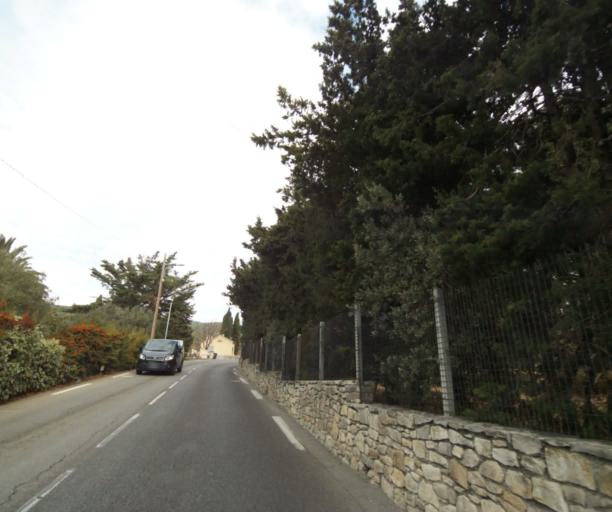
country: FR
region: Provence-Alpes-Cote d'Azur
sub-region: Departement des Bouches-du-Rhone
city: Ceyreste
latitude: 43.2190
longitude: 5.6400
